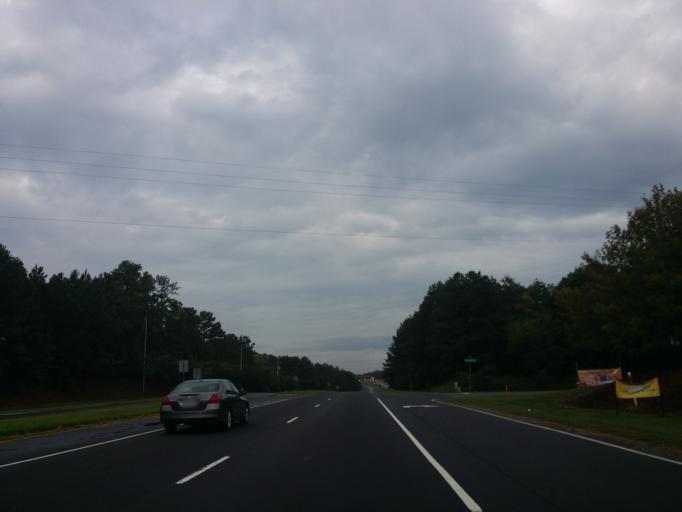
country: US
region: North Carolina
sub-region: Wake County
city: Morrisville
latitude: 35.9189
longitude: -78.8034
